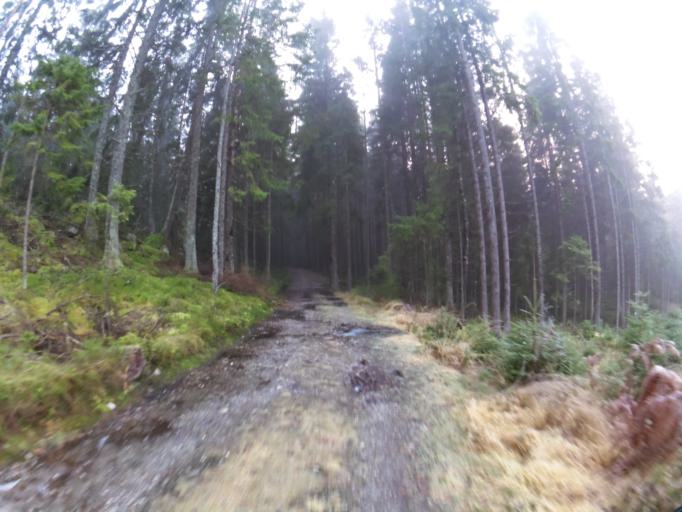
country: NO
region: Ostfold
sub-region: Fredrikstad
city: Fredrikstad
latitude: 59.2684
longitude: 10.9758
